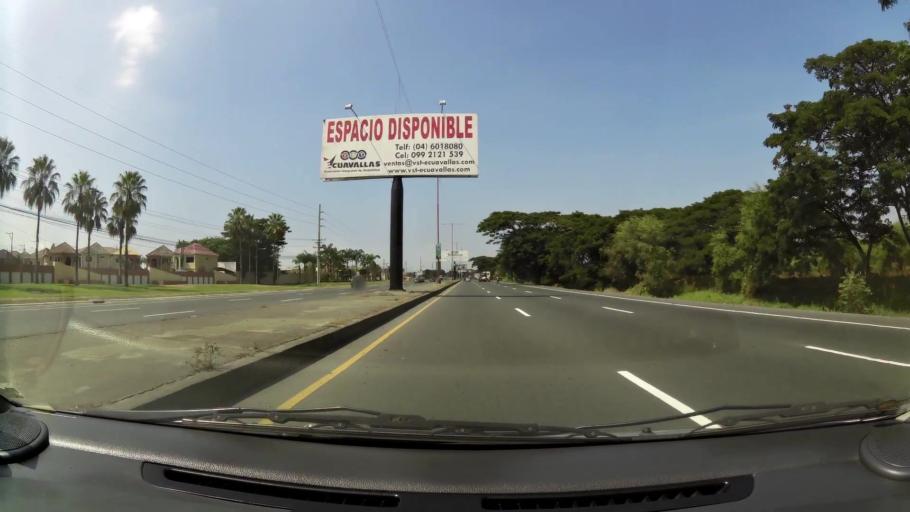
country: EC
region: Guayas
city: Eloy Alfaro
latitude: -2.0516
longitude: -79.8926
